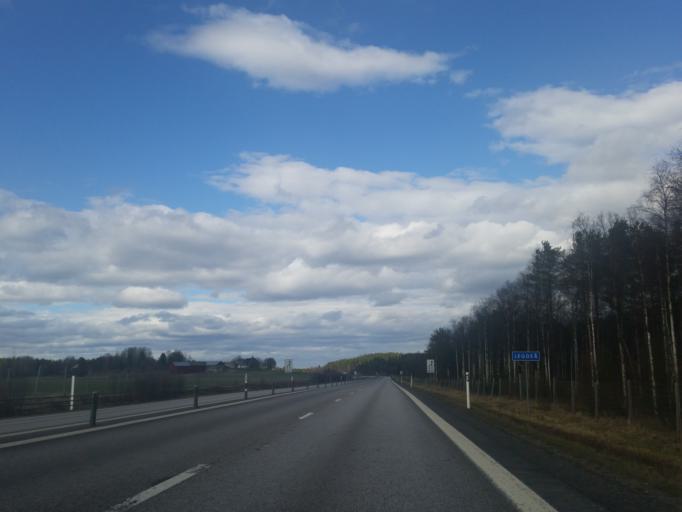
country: SE
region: Vaesterbotten
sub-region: Robertsfors Kommun
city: Robertsfors
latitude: 64.1499
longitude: 20.9062
